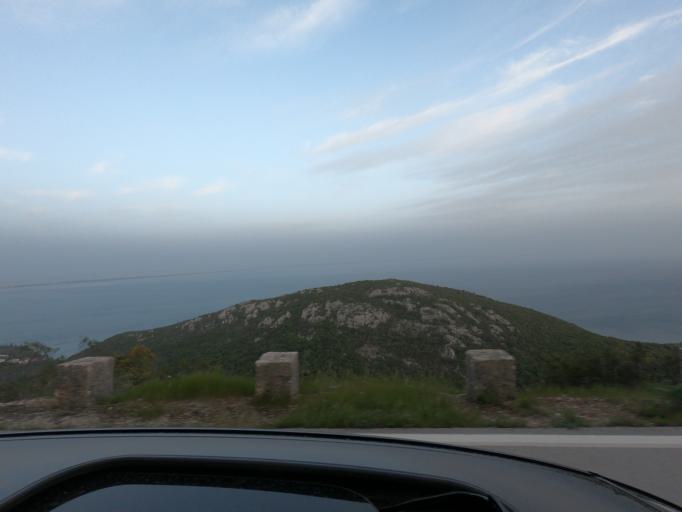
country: PT
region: Setubal
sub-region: Sesimbra
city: Sesimbra
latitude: 38.4651
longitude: -9.0030
